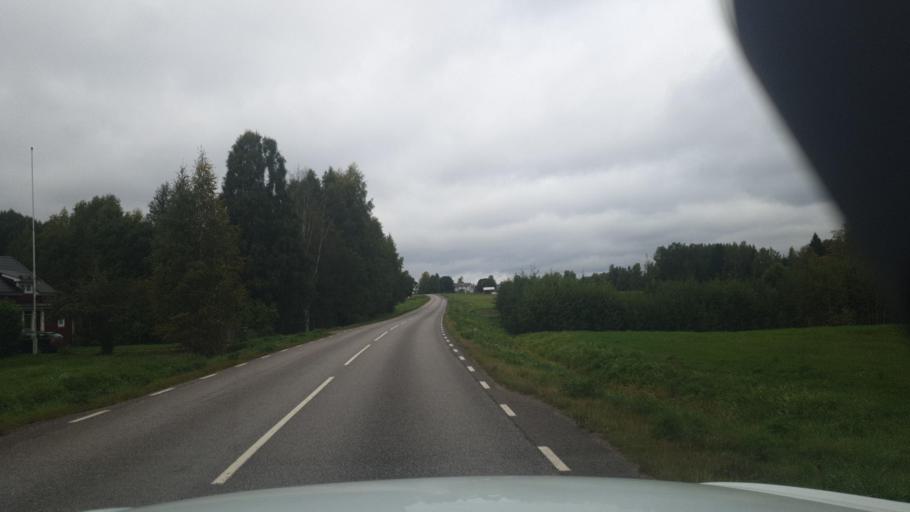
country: SE
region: Vaermland
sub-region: Sunne Kommun
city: Sunne
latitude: 59.8078
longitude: 13.0333
